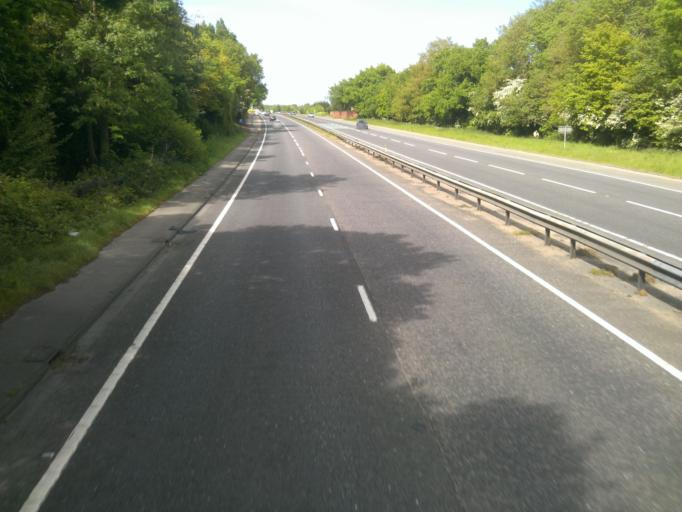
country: GB
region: England
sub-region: Suffolk
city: East Bergholt
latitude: 51.9456
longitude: 0.9573
